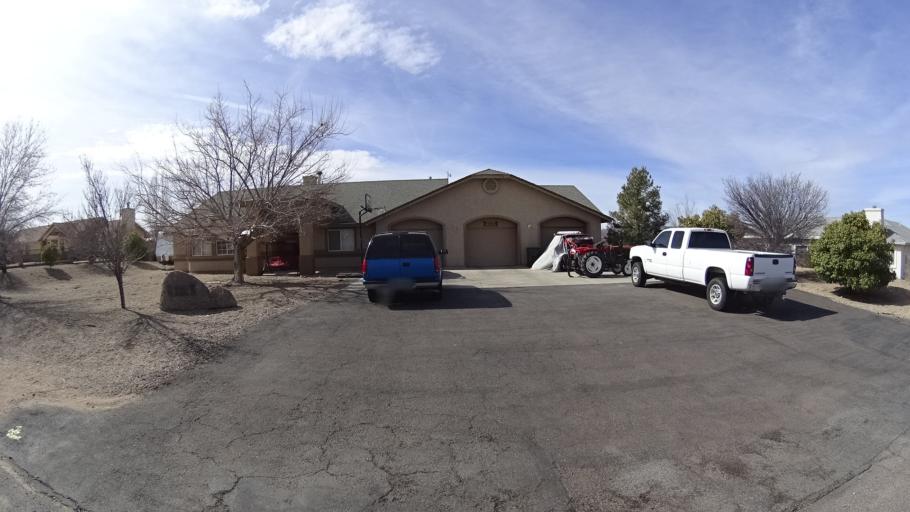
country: US
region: Arizona
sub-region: Mohave County
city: Kingman
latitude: 35.1953
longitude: -113.9901
